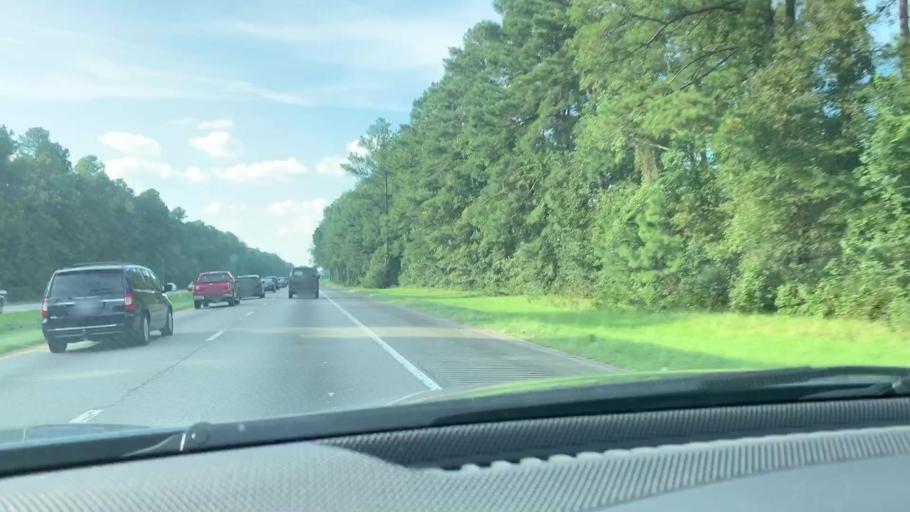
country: US
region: South Carolina
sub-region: Orangeburg County
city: Brookdale
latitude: 33.5115
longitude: -80.7819
